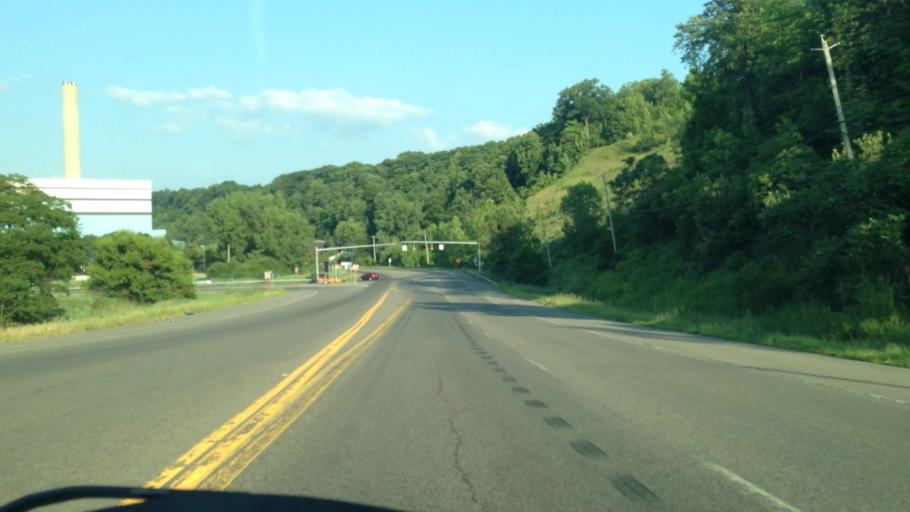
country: US
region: New York
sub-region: Onondaga County
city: Nedrow
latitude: 43.0058
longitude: -76.1204
